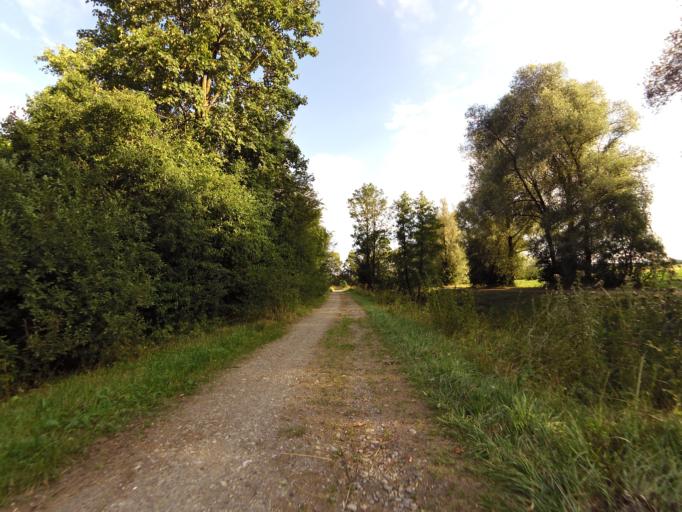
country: CH
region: Zurich
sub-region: Bezirk Buelach
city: Bachenbulach
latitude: 47.4803
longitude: 8.5436
